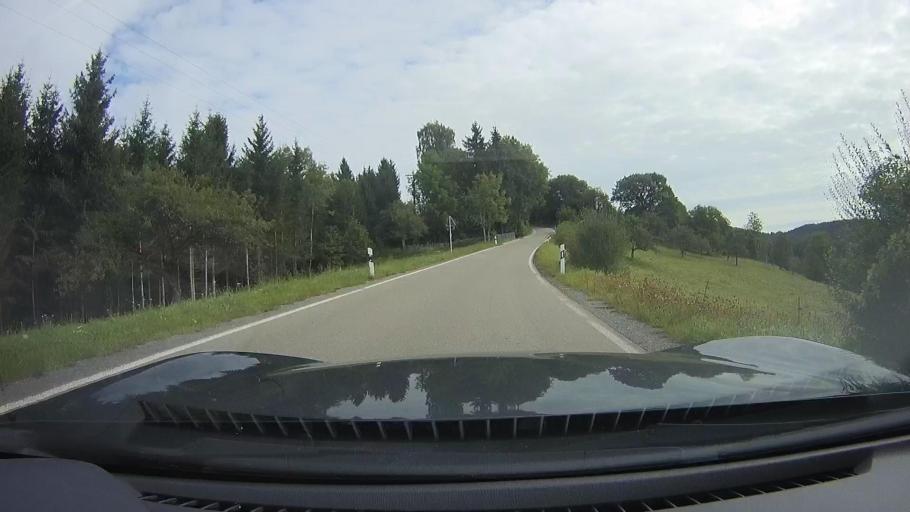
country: DE
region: Baden-Wuerttemberg
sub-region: Regierungsbezirk Stuttgart
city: Wustenrot
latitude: 49.0648
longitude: 9.4514
